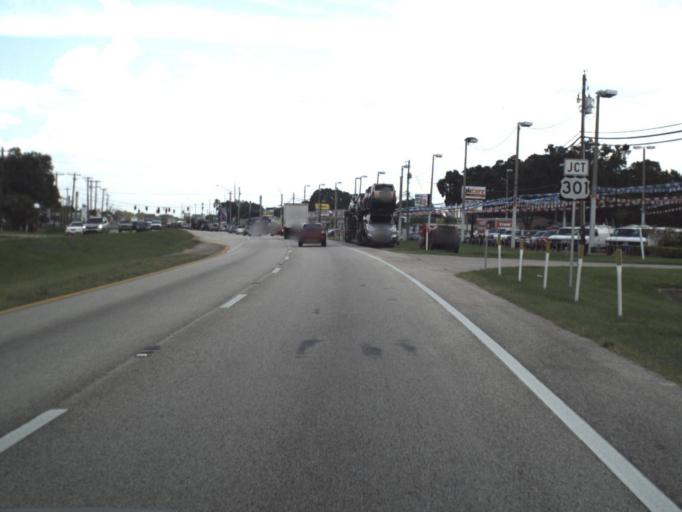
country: US
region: Florida
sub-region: Hillsborough County
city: Palm River-Clair Mel
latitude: 27.9493
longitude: -82.3580
